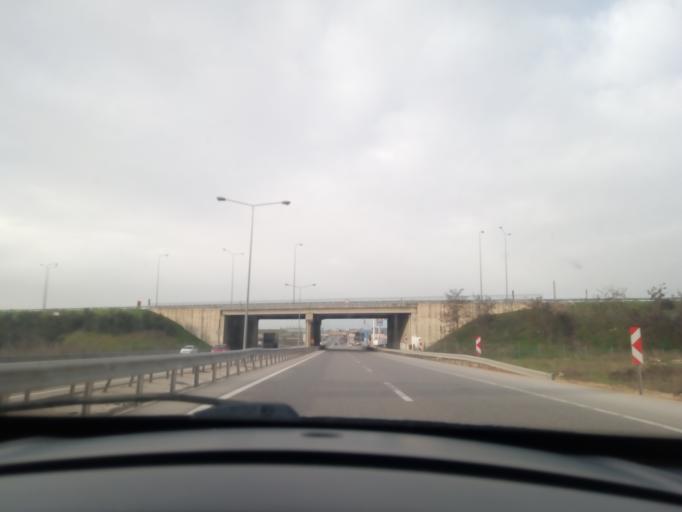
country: TR
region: Bursa
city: Gorukle
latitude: 40.2244
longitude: 28.7809
